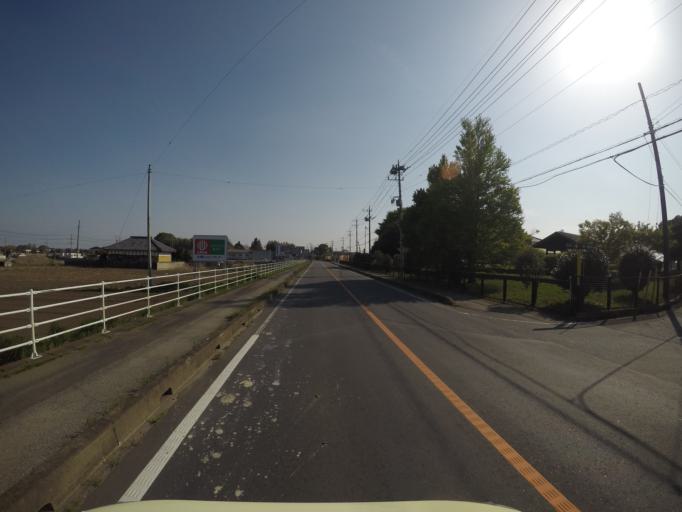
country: JP
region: Ibaraki
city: Yuki
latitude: 36.2837
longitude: 139.8800
